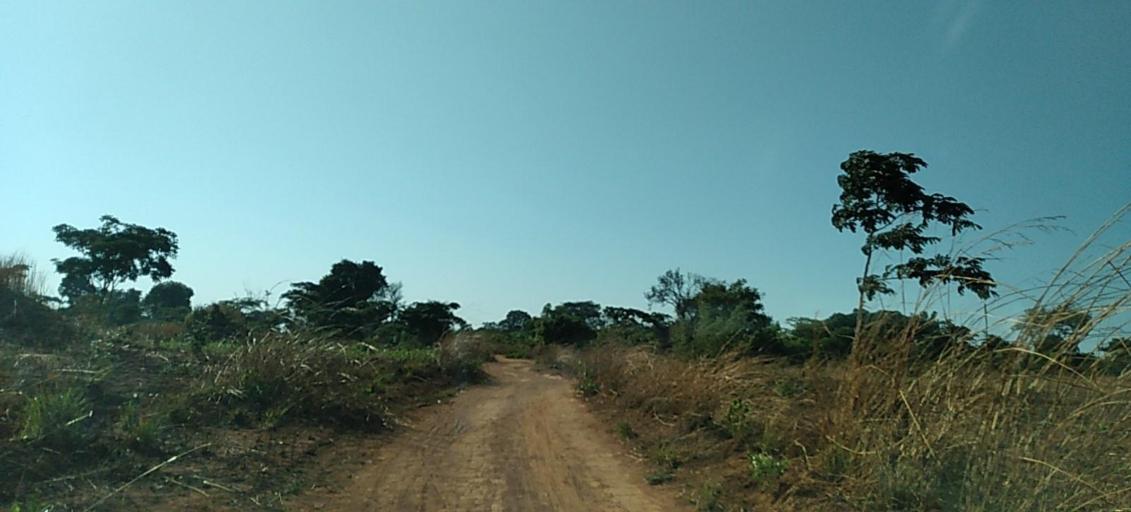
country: ZM
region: Copperbelt
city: Chililabombwe
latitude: -12.3694
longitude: 27.9005
